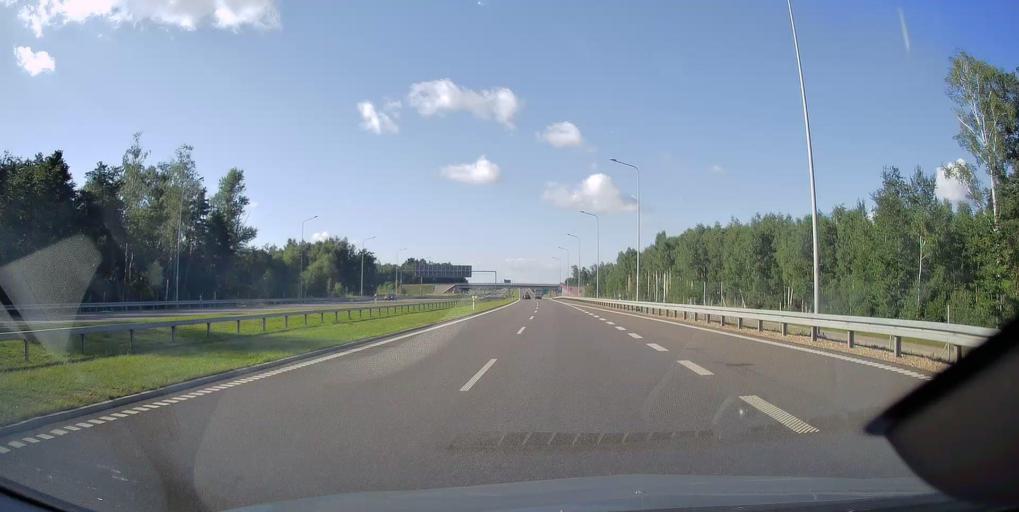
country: PL
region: Masovian Voivodeship
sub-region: Powiat szydlowiecki
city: Oronsko
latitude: 51.3439
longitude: 21.0157
